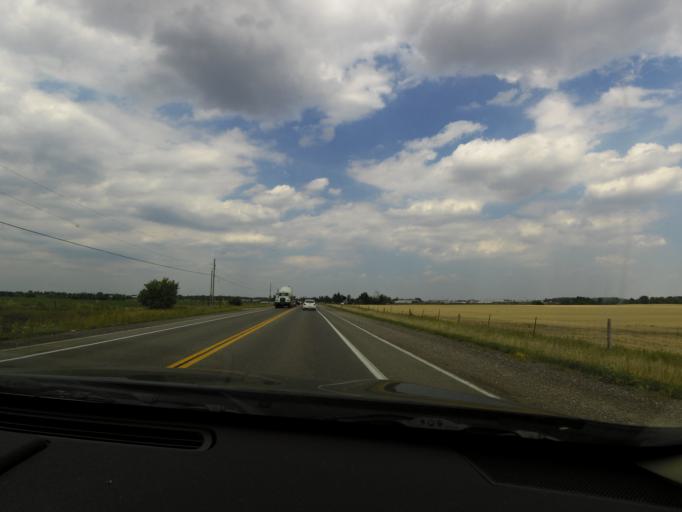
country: CA
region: Ontario
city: Brampton
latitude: 43.7652
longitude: -79.8873
